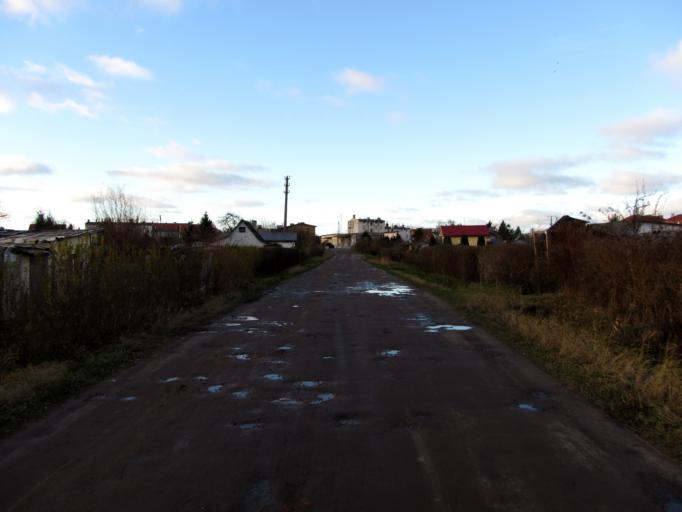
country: PL
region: West Pomeranian Voivodeship
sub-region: Powiat kolobrzeski
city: Kolobrzeg
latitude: 54.1659
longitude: 15.5732
